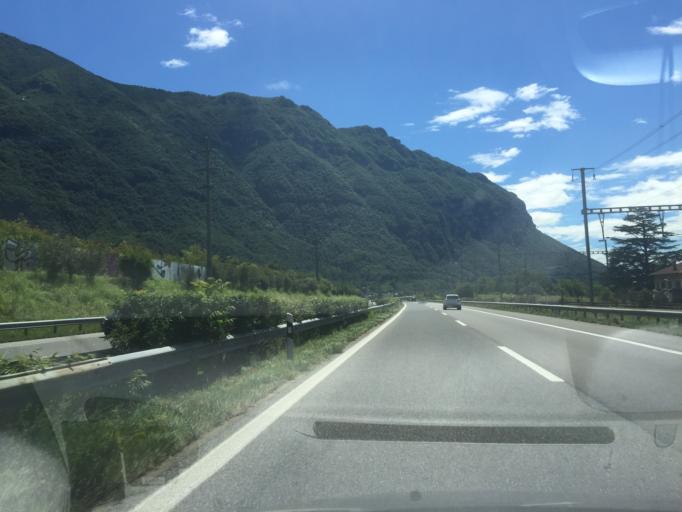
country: CH
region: Ticino
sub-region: Lugano District
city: Melano
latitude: 45.9291
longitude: 8.9776
